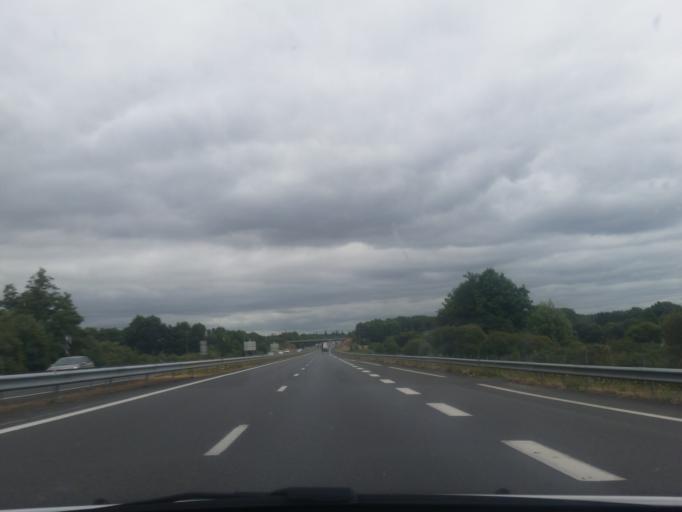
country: FR
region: Pays de la Loire
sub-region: Departement de la Sarthe
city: Parce-sur-Sarthe
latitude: 47.8105
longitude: -0.1630
